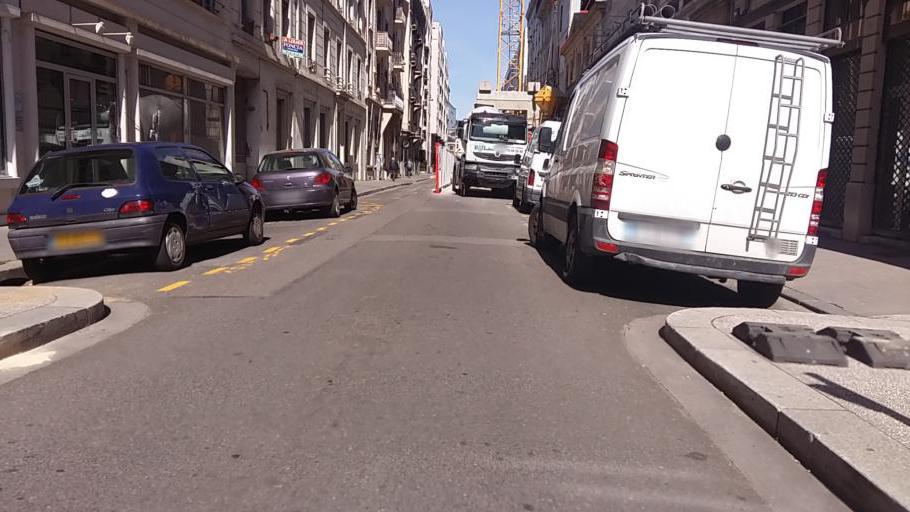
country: FR
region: Rhone-Alpes
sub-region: Departement du Rhone
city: Lyon
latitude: 45.7475
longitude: 4.8350
